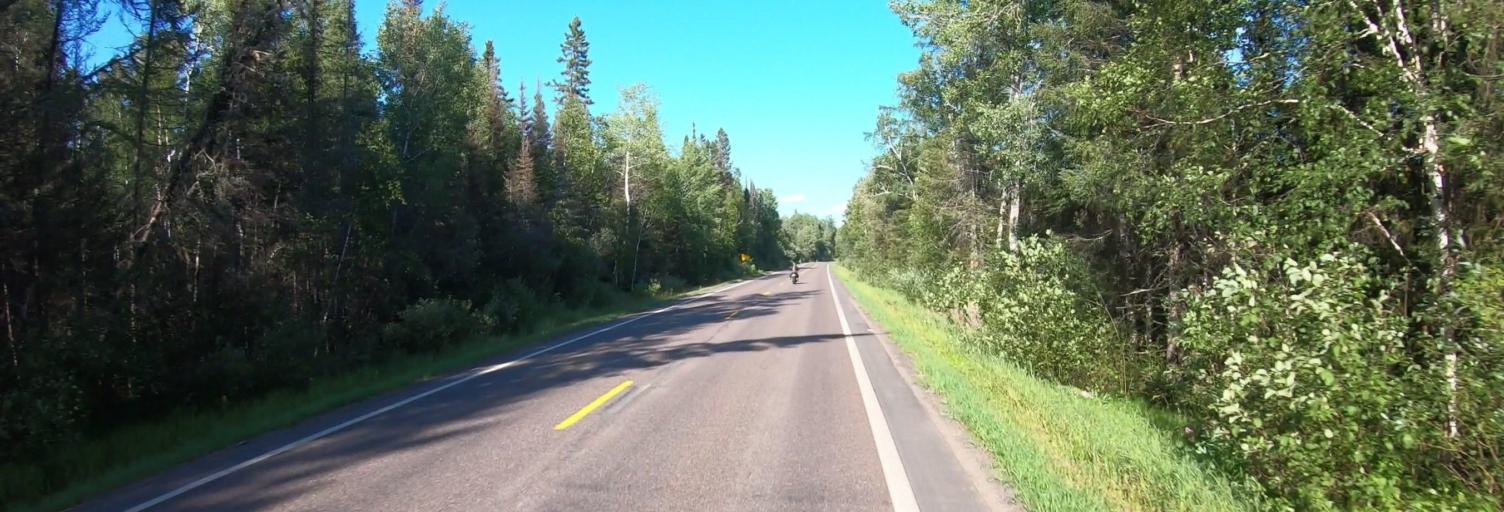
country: US
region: Minnesota
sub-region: Saint Louis County
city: Ely
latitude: 47.9335
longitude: -91.7004
